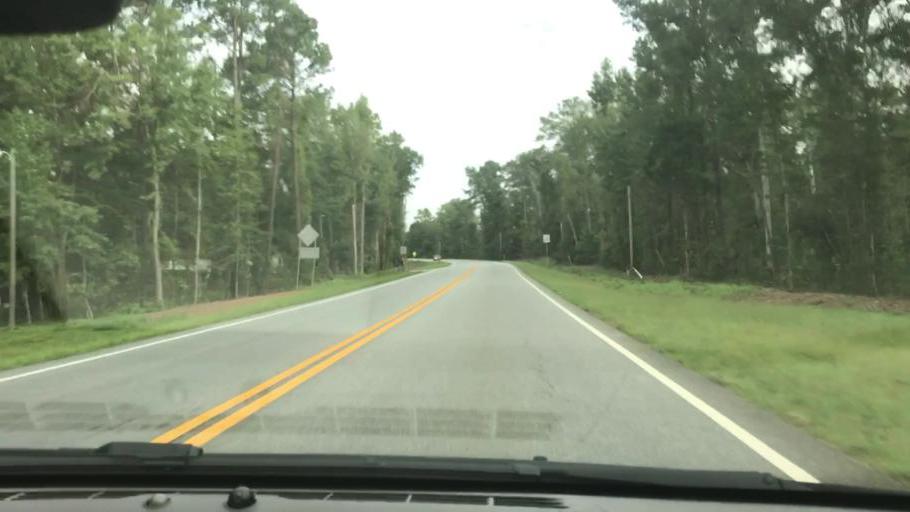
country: US
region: Georgia
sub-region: Quitman County
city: Georgetown
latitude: 31.8773
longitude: -85.0823
